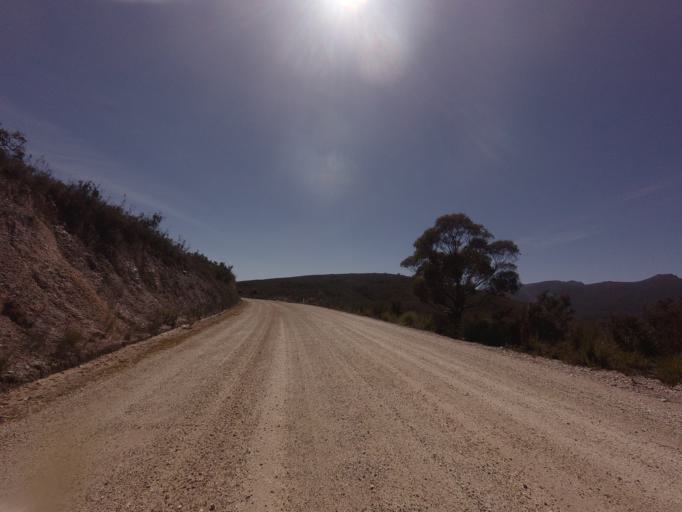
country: AU
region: Tasmania
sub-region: Huon Valley
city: Geeveston
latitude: -43.0363
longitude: 146.3330
